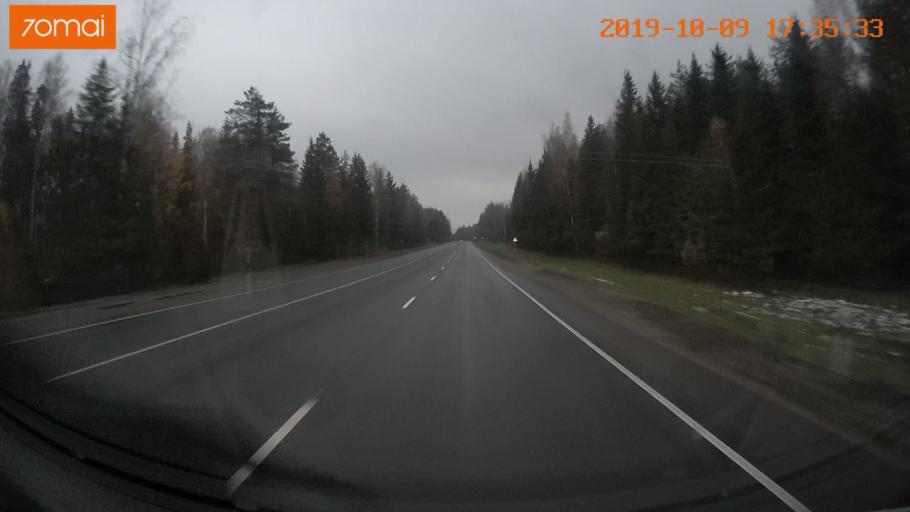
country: RU
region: Ivanovo
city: Bogorodskoye
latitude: 57.0918
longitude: 41.0014
